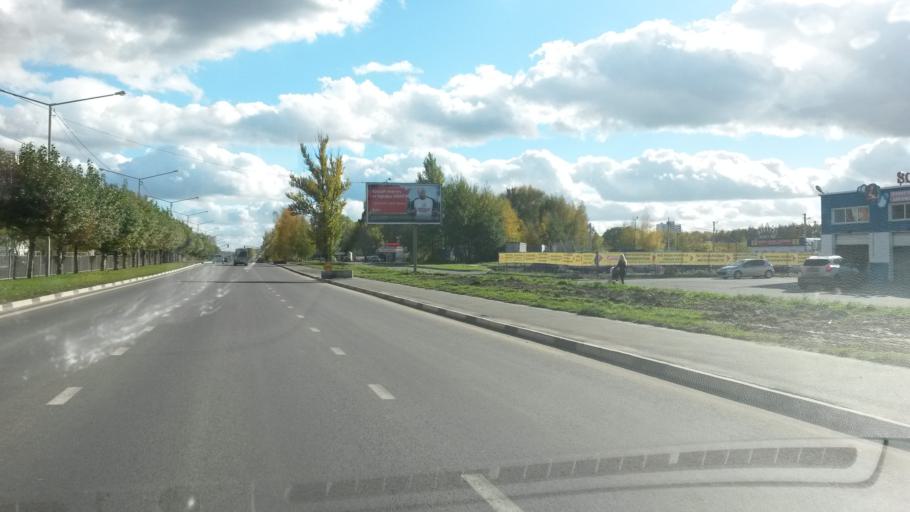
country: RU
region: Jaroslavl
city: Yaroslavl
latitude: 57.5796
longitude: 39.9128
